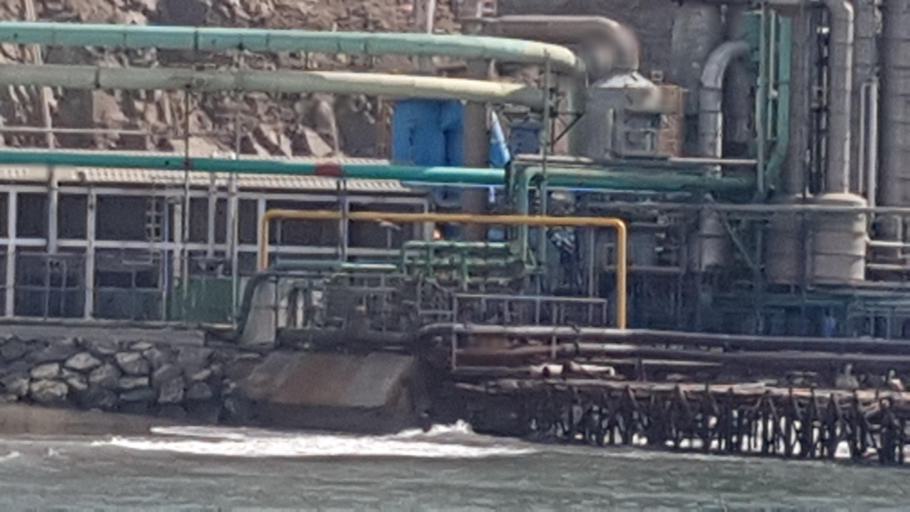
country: PE
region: Ancash
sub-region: Provincia de Santa
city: Coishco
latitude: -9.0189
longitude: -78.6230
